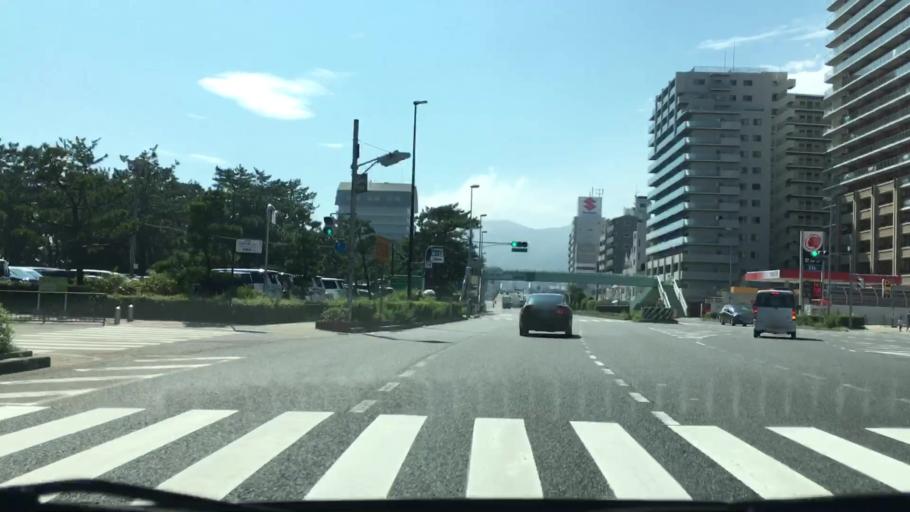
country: JP
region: Hyogo
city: Kobe
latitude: 34.6445
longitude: 135.1267
